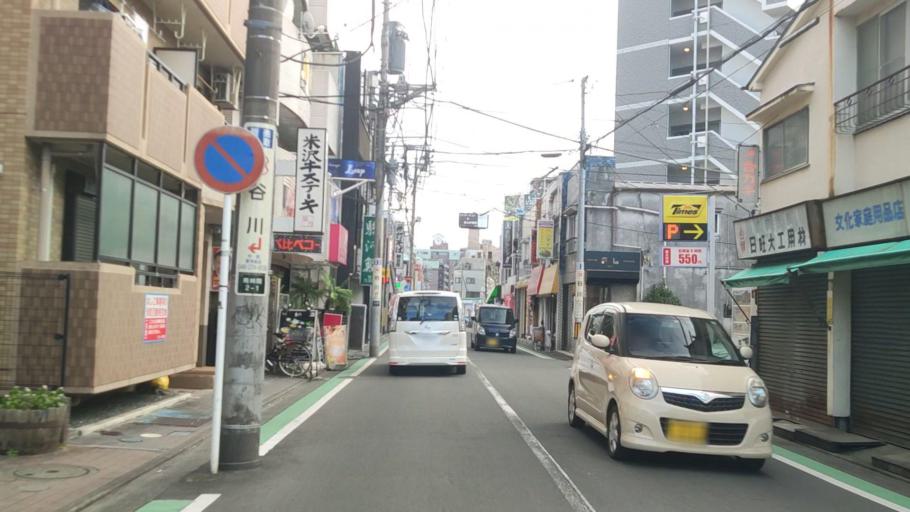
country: JP
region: Kanagawa
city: Minami-rinkan
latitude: 35.4966
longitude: 139.4467
